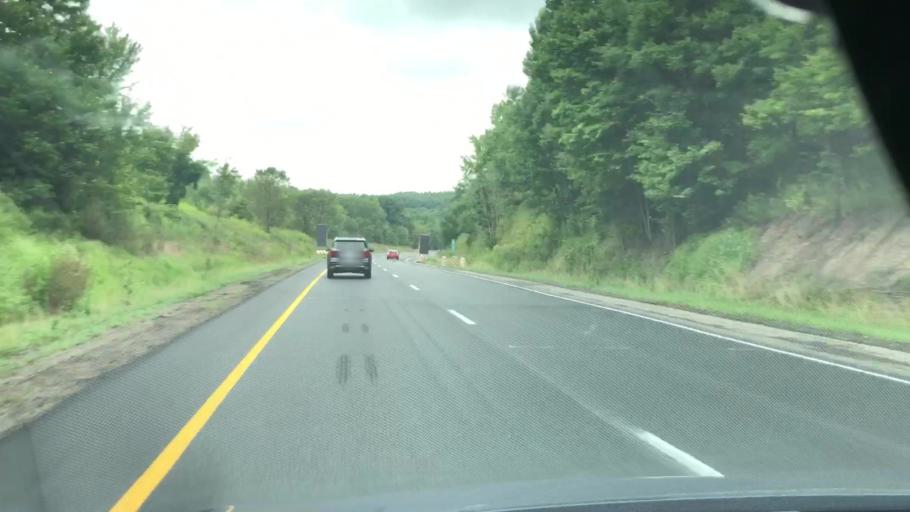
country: US
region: Pennsylvania
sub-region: Butler County
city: Prospect
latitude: 40.8969
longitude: -80.1222
